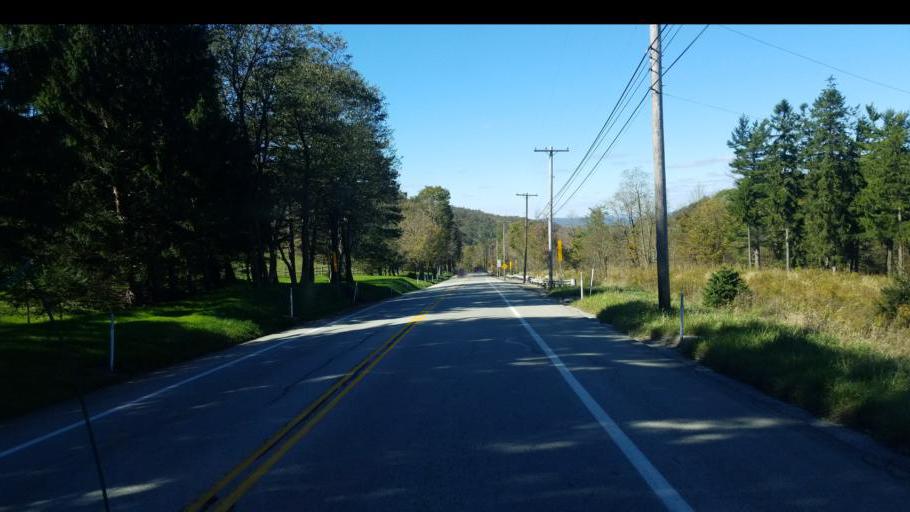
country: US
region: Pennsylvania
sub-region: Westmoreland County
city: Waterford
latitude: 40.1836
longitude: -79.1422
